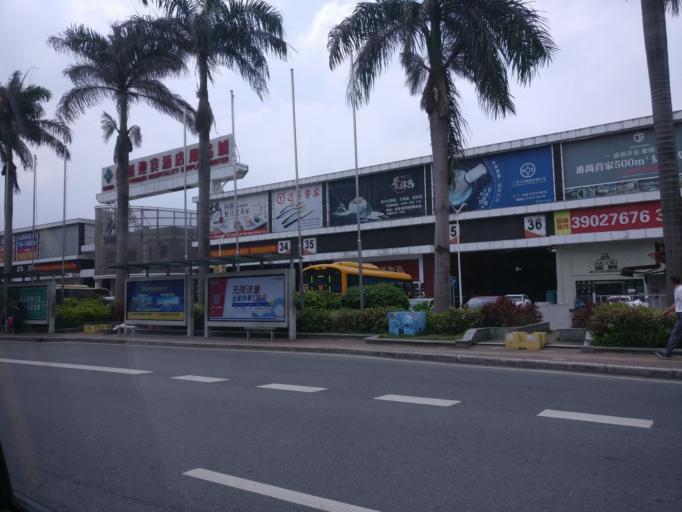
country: CN
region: Guangdong
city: Dashi
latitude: 23.0386
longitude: 113.3130
